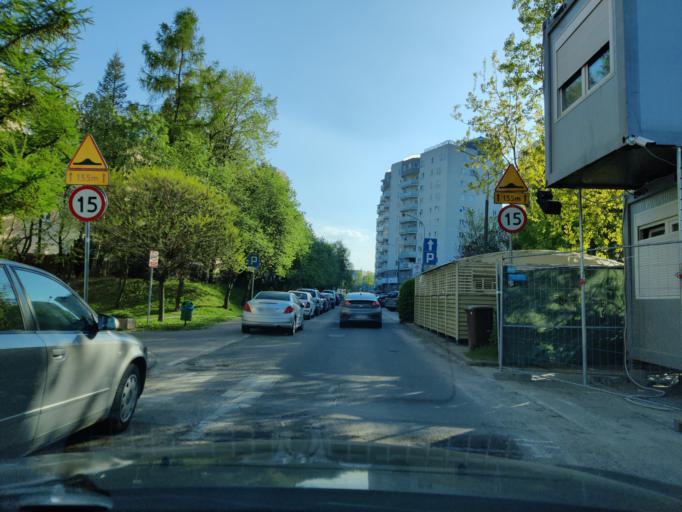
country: PL
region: Masovian Voivodeship
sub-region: Warszawa
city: Ursynow
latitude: 52.1401
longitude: 21.0612
